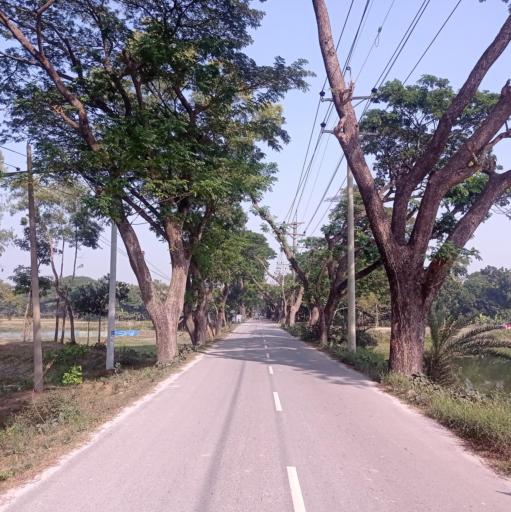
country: BD
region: Dhaka
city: Narsingdi
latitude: 24.0556
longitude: 90.6847
